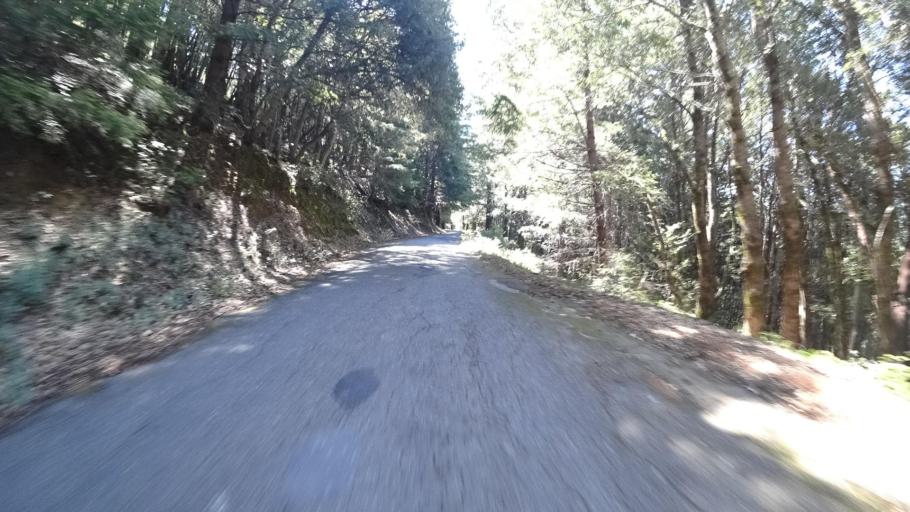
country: US
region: California
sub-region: Humboldt County
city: Redway
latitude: 40.1716
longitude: -124.0881
